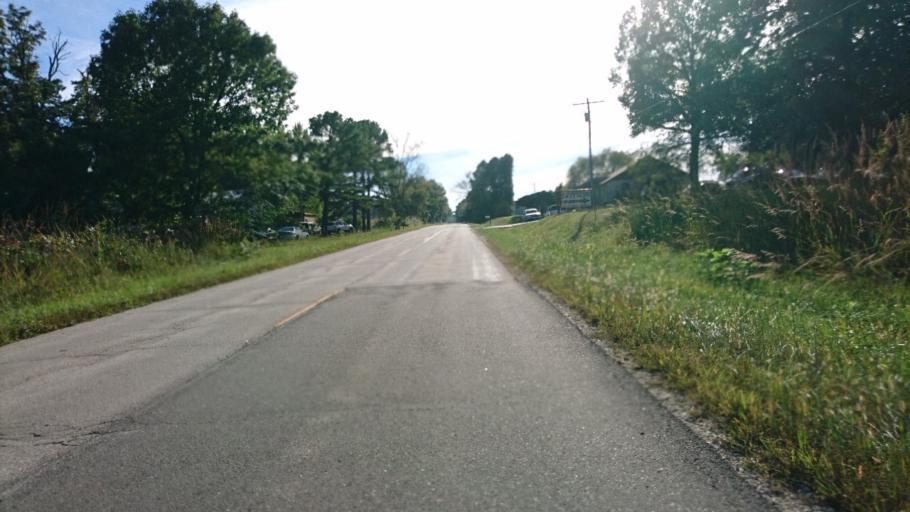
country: US
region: Missouri
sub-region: Crawford County
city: Cuba
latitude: 38.1054
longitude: -91.3440
